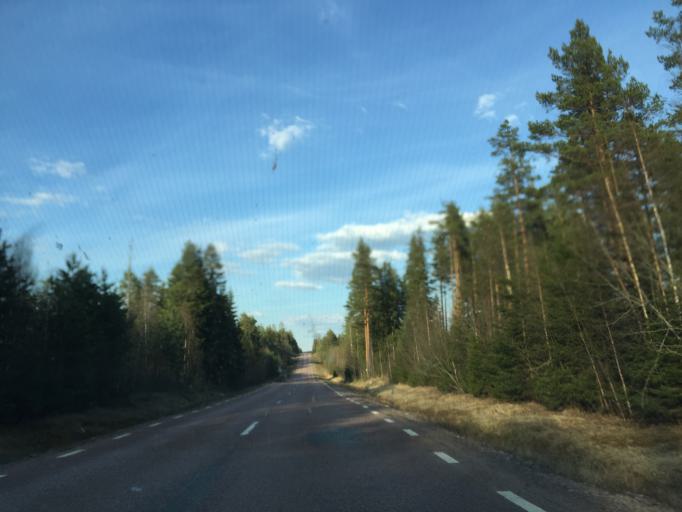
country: SE
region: Dalarna
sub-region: Leksand Municipality
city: Siljansnas
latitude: 60.6737
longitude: 14.6754
